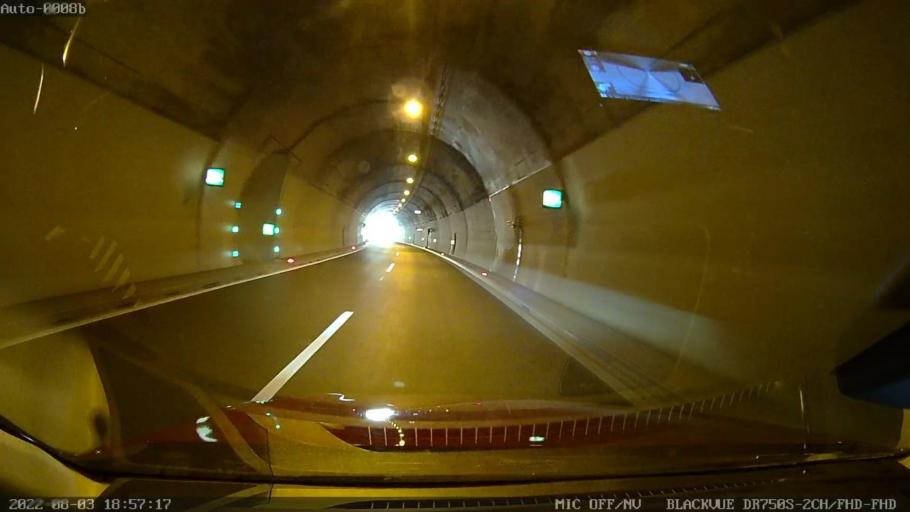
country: SI
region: Vipava
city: Vipava
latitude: 45.7997
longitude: 13.9819
